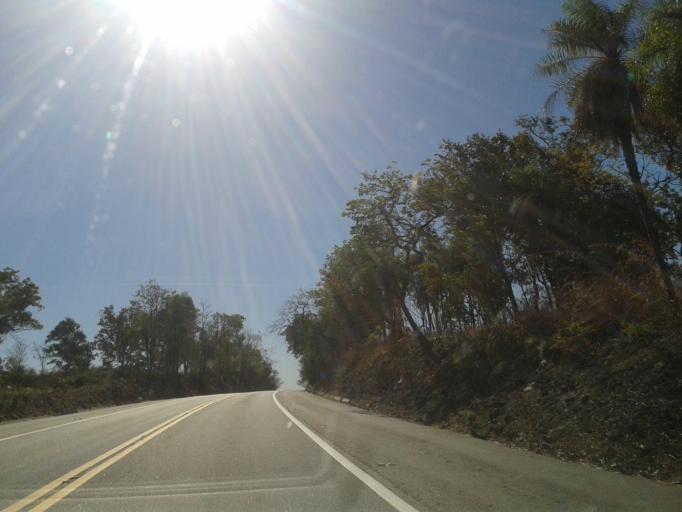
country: BR
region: Goias
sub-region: Goias
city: Goias
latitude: -15.7644
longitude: -50.1564
